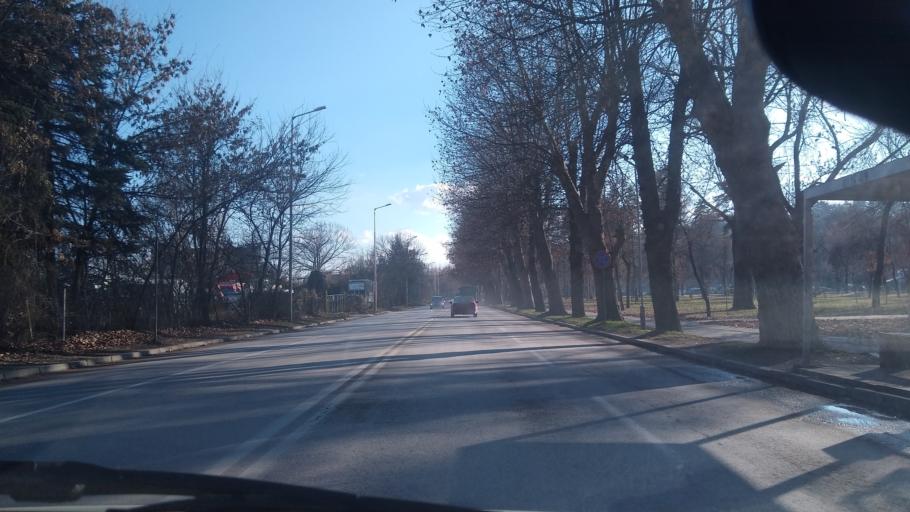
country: MK
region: Bitola
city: Bitola
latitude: 41.0195
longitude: 21.3414
